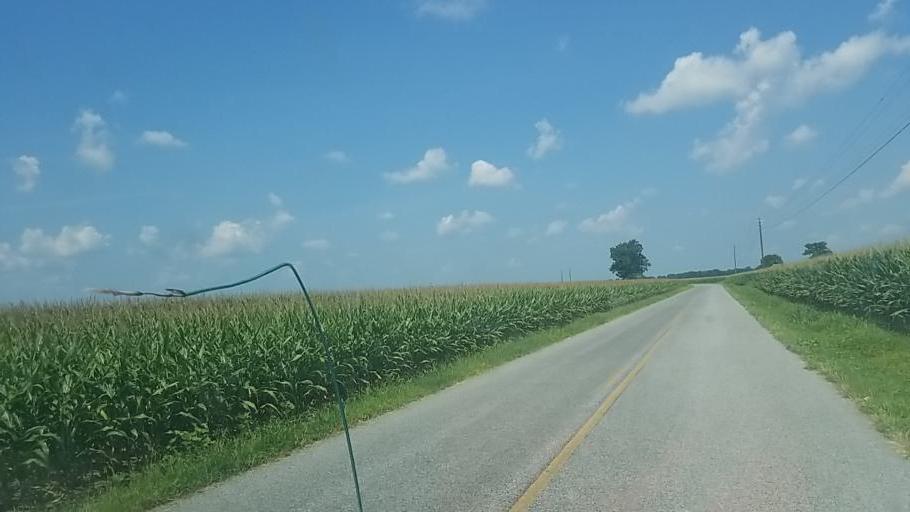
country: US
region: Maryland
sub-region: Worcester County
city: Berlin
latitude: 38.2923
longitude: -75.2467
